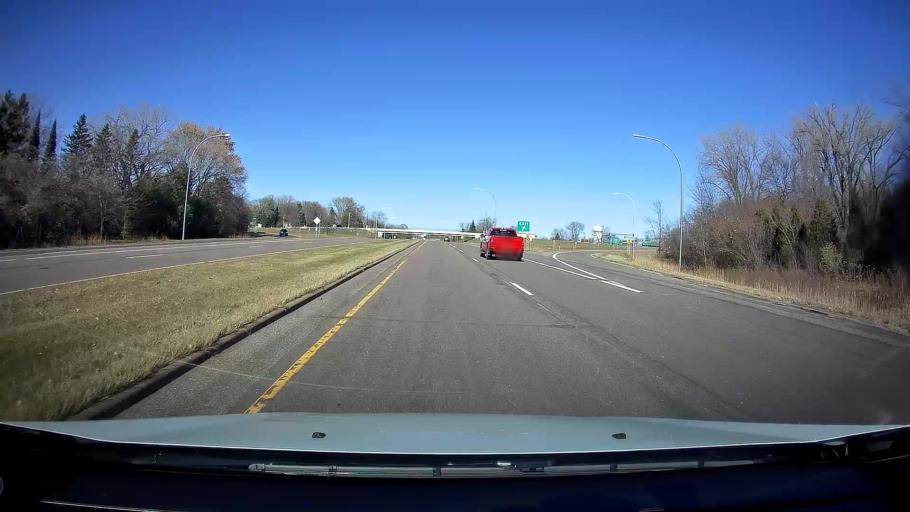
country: US
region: Minnesota
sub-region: Ramsey County
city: Arden Hills
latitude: 45.0485
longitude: -93.1556
